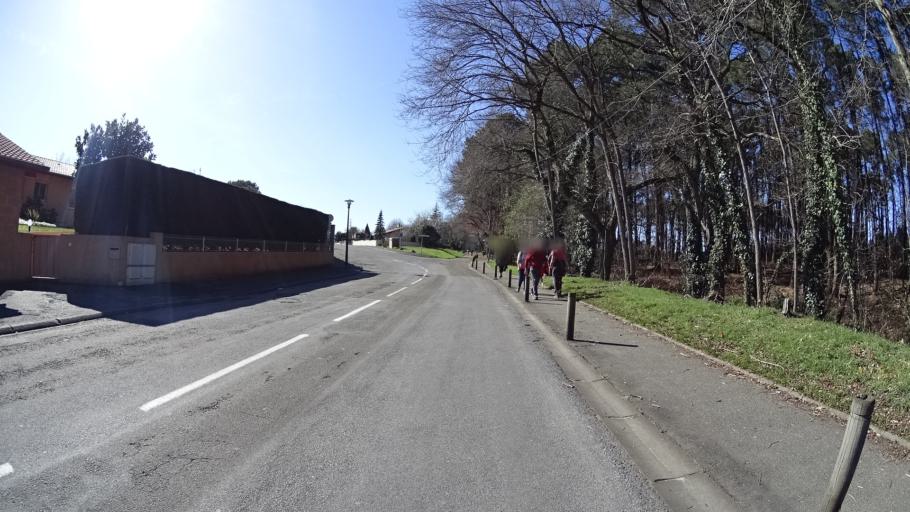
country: FR
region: Aquitaine
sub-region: Departement des Landes
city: Saint-Paul-les-Dax
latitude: 43.7341
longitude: -1.0759
